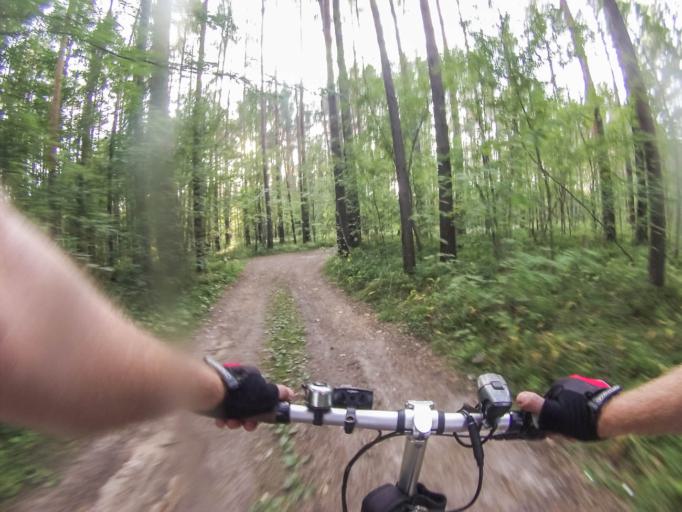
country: RU
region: Jaroslavl
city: Myshkin
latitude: 57.7599
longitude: 38.4467
